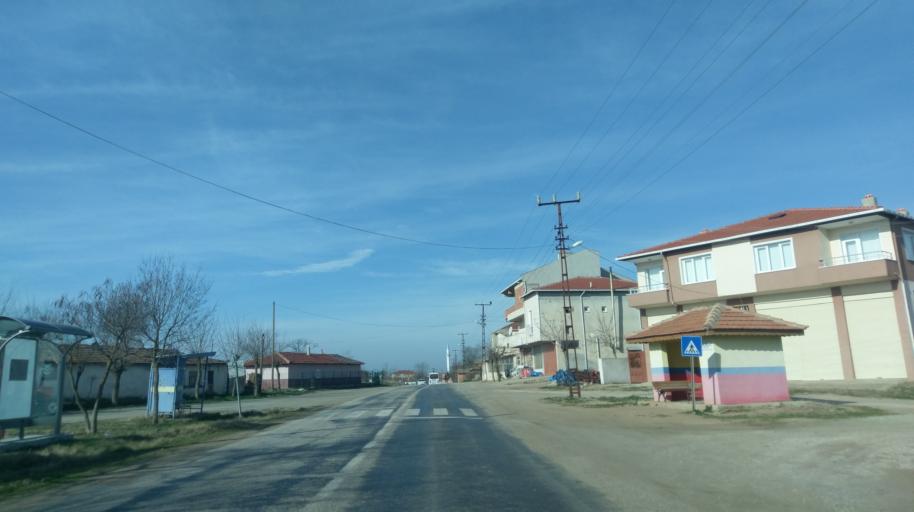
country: TR
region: Edirne
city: Copkoy
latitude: 41.3071
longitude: 26.8256
